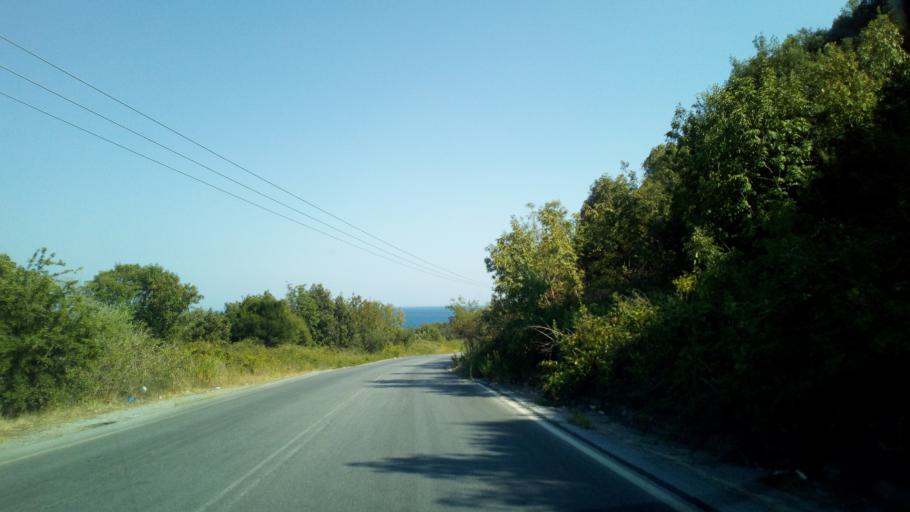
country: GR
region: Central Macedonia
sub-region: Nomos Thessalonikis
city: Stavros
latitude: 40.6516
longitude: 23.7421
